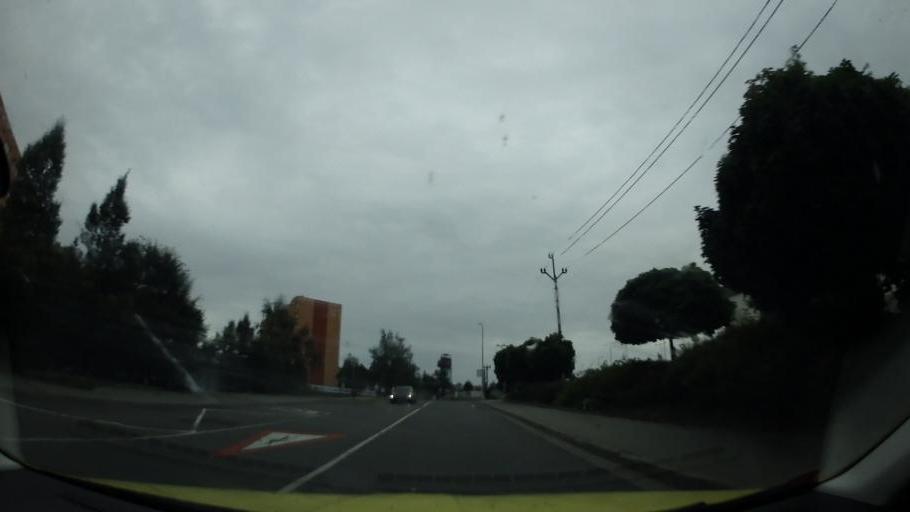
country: CZ
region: Olomoucky
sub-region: Okres Prerov
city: Hranice
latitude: 49.5592
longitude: 17.7472
